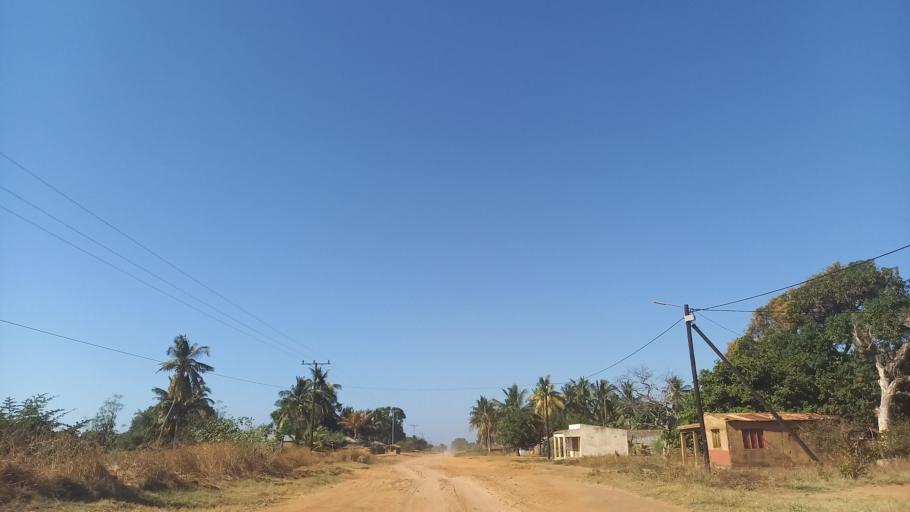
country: MZ
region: Cabo Delgado
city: Pemba
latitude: -13.1455
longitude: 40.5564
